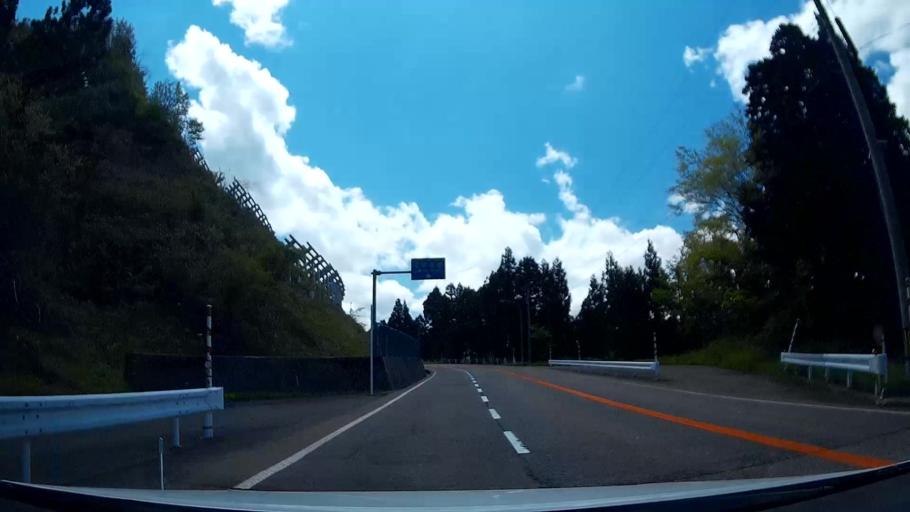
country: JP
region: Toyama
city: Fukumitsu
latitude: 36.4749
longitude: 136.8943
